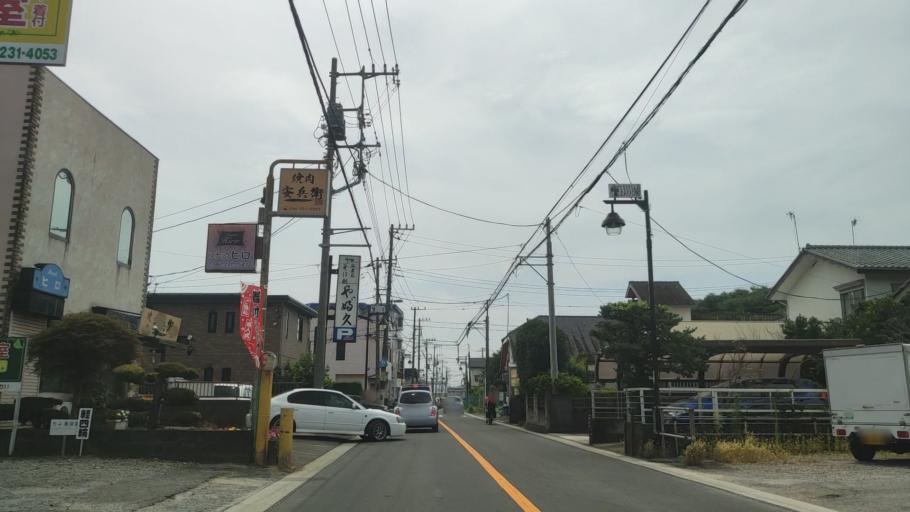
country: JP
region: Kanagawa
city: Zama
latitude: 35.4607
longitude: 139.3985
